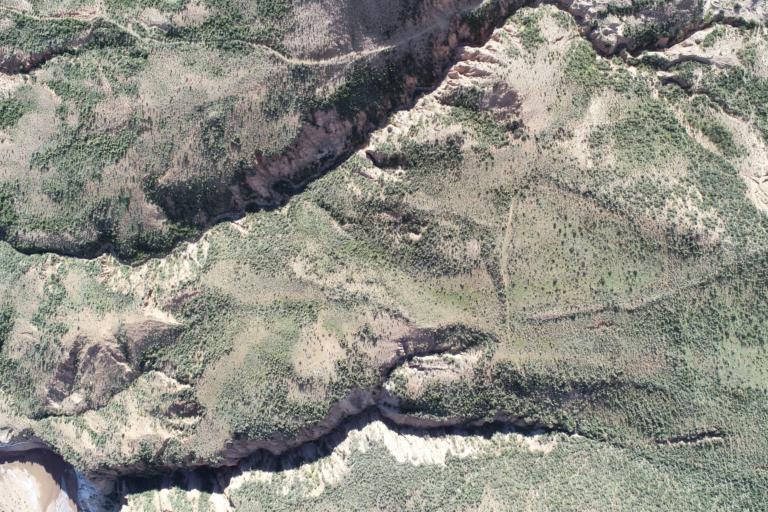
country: BO
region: La Paz
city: Curahuara de Carangas
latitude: -17.3017
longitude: -68.4945
